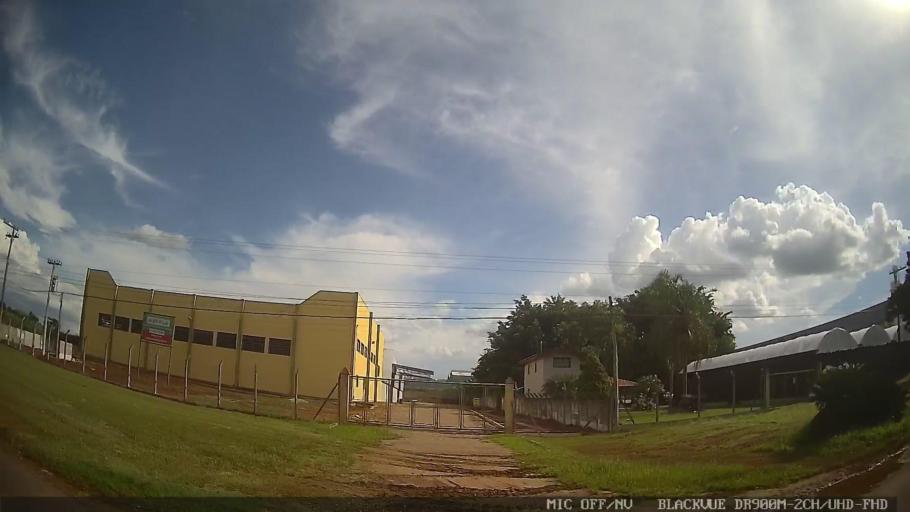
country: BR
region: Sao Paulo
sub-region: Laranjal Paulista
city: Laranjal Paulista
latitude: -23.0369
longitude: -47.8743
